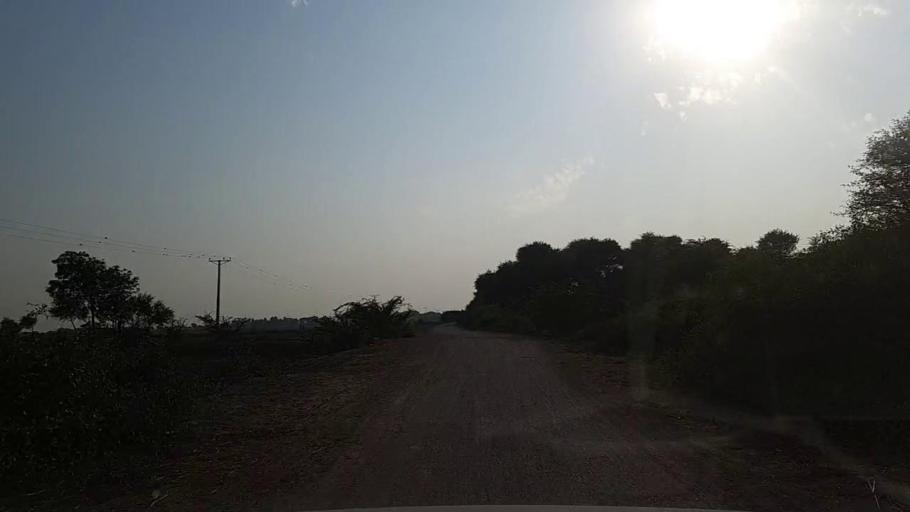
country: PK
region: Sindh
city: Mirpur Batoro
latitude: 24.7827
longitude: 68.2449
